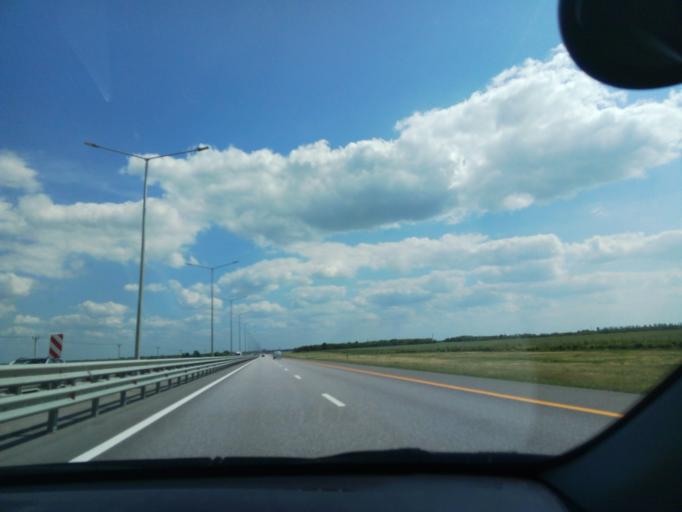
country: RU
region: Voronezj
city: Podkletnoye
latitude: 51.5045
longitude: 39.5182
